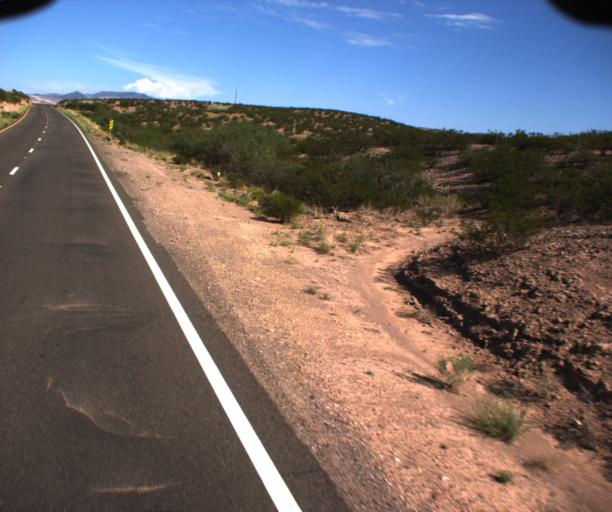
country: US
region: Arizona
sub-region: Greenlee County
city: Clifton
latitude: 32.9904
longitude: -109.2685
